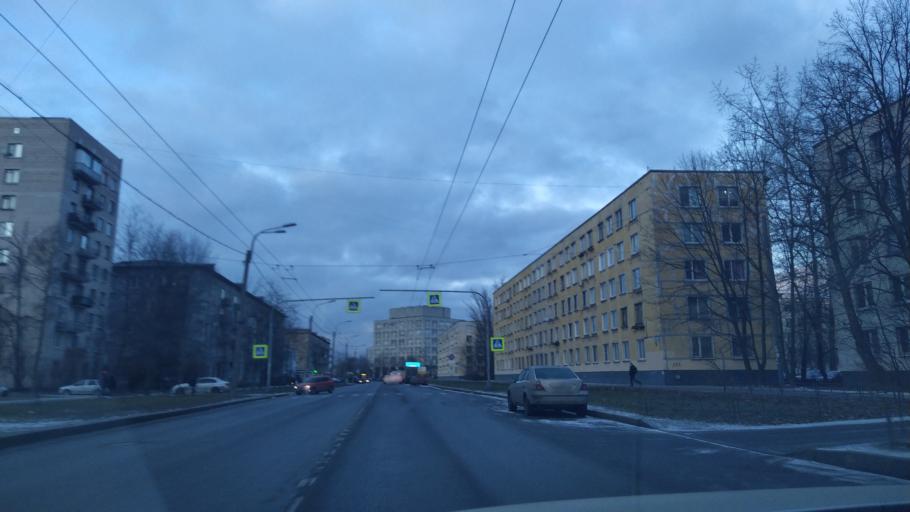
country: RU
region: St.-Petersburg
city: Dachnoye
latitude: 59.8544
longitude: 30.2563
